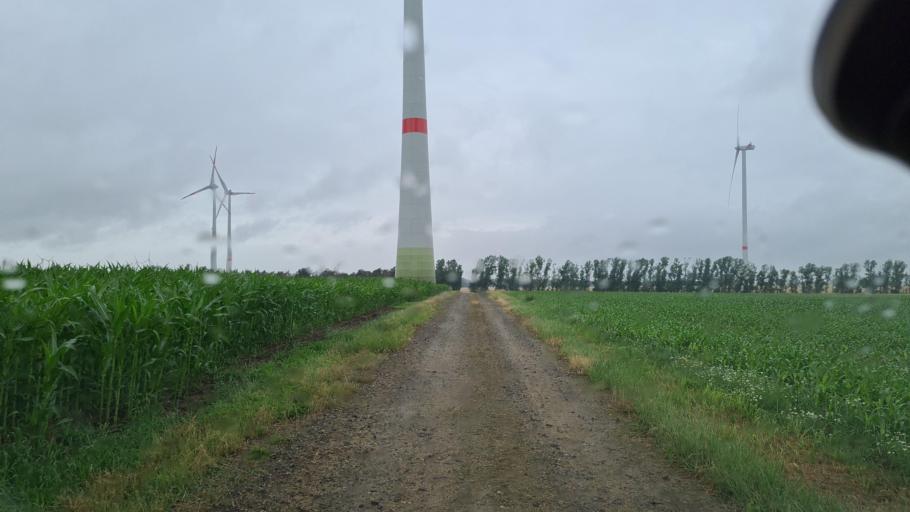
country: DE
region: Brandenburg
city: Juterbog
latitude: 51.9518
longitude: 13.1748
